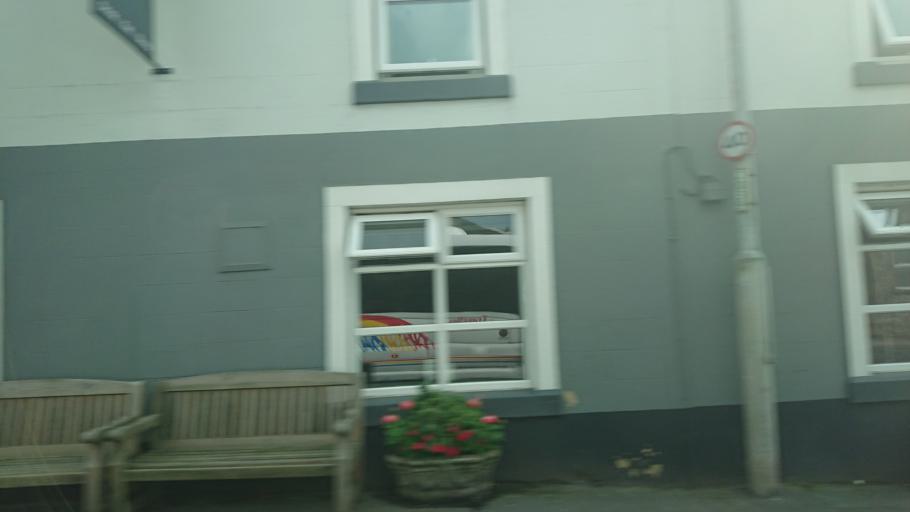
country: GB
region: England
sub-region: North Yorkshire
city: Ingleton
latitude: 54.1483
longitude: -2.4744
